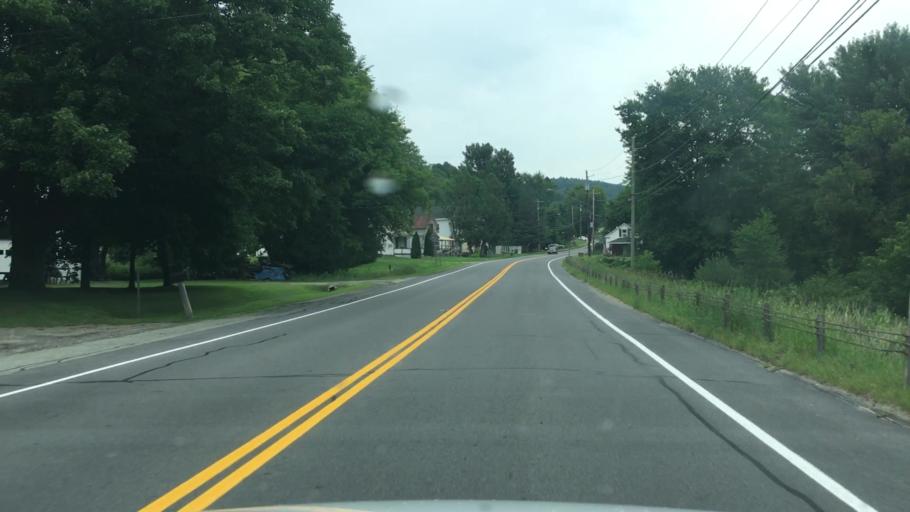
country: US
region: New York
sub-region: Essex County
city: Keeseville
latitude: 44.4654
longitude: -73.5863
